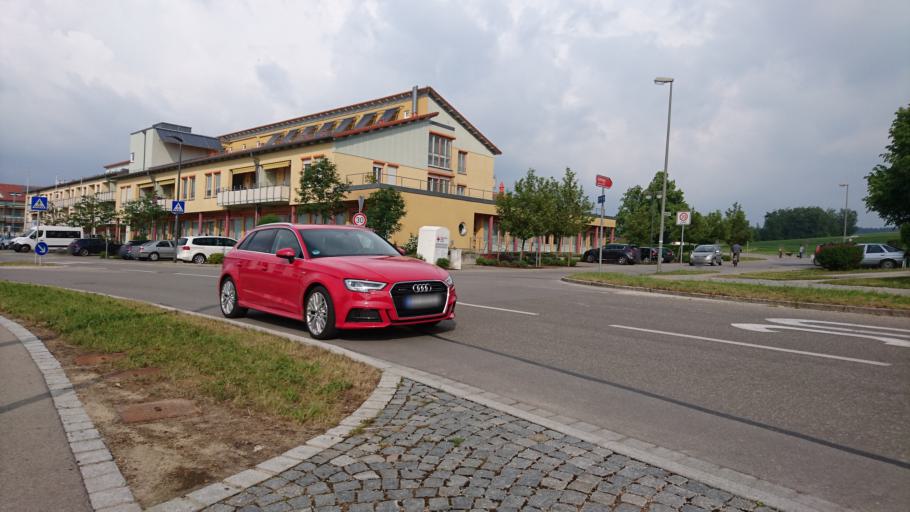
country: DE
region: Bavaria
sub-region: Swabia
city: Diedorf
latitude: 48.3563
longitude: 10.7872
